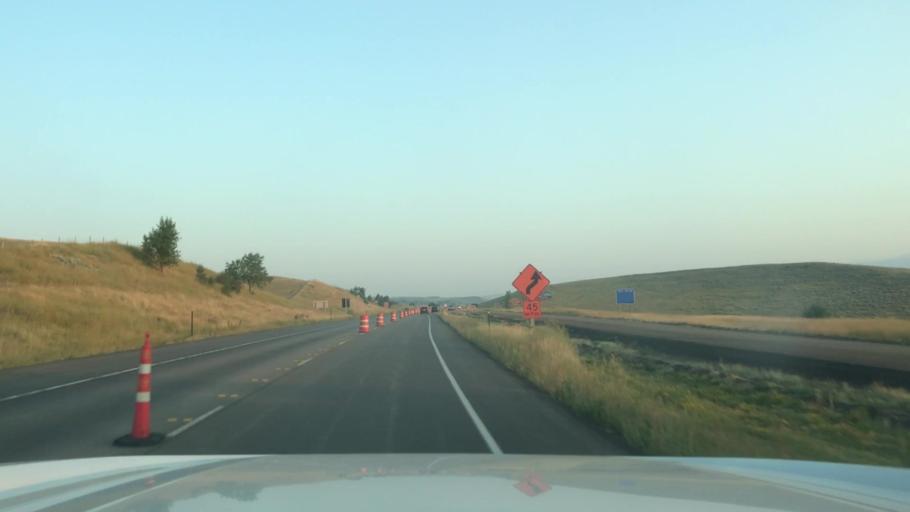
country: US
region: Wyoming
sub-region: Sheridan County
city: Sheridan
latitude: 44.8182
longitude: -106.9399
